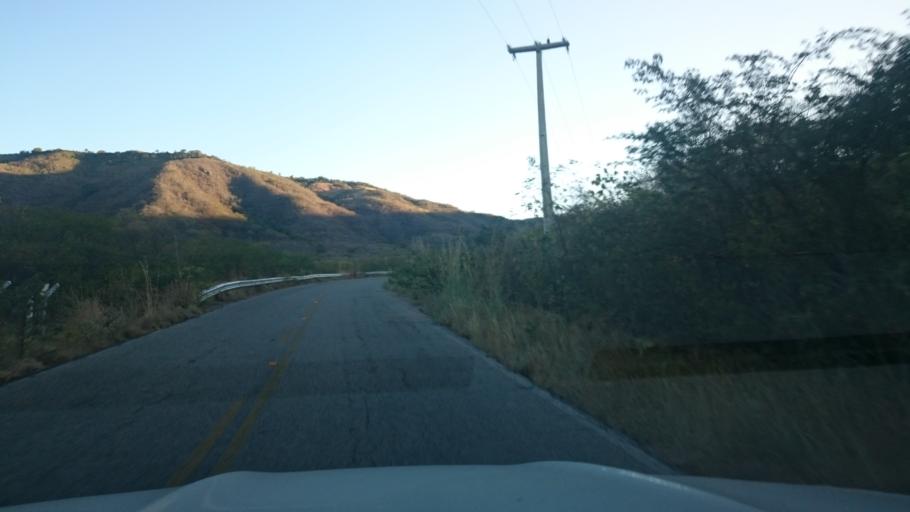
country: BR
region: Rio Grande do Norte
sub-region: Umarizal
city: Umarizal
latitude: -6.0079
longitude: -37.9787
